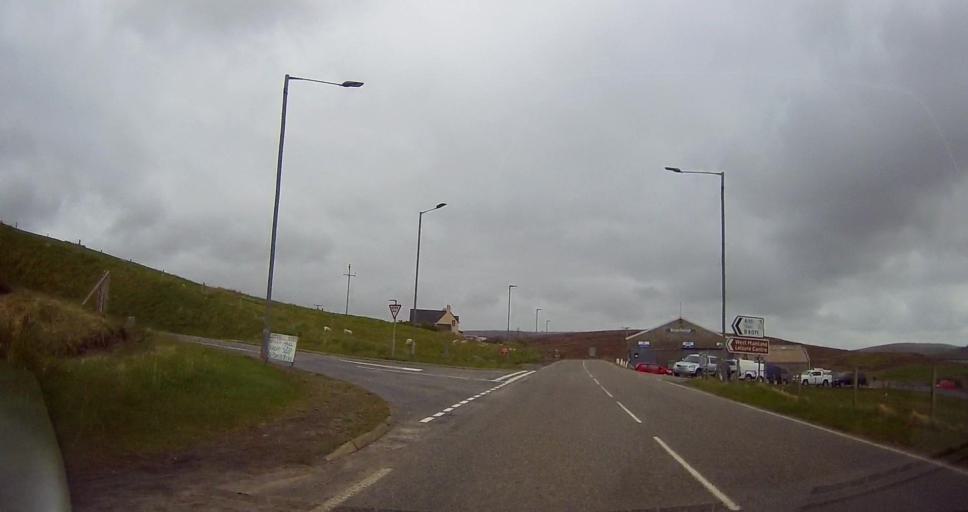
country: GB
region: Scotland
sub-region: Shetland Islands
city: Lerwick
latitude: 60.2542
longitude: -1.4054
